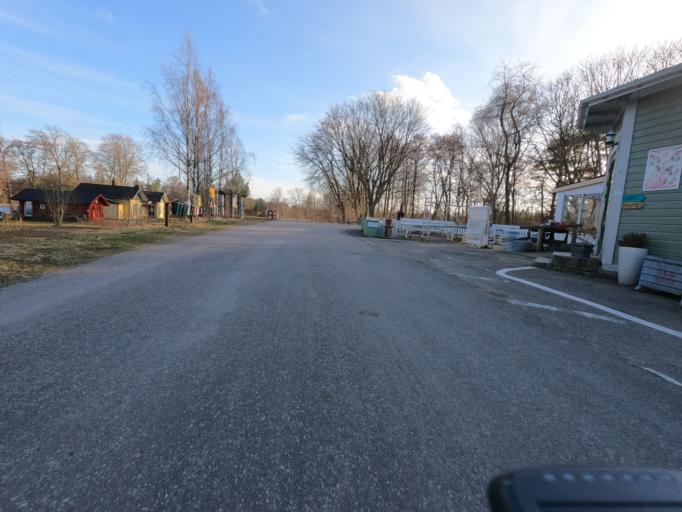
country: SE
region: Blekinge
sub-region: Karlshamns Kommun
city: Svangsta
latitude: 56.5288
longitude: 14.6740
